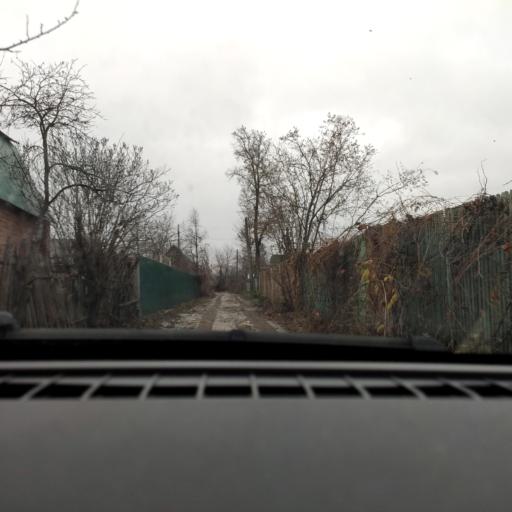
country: RU
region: Voronezj
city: Maslovka
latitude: 51.6112
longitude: 39.2744
